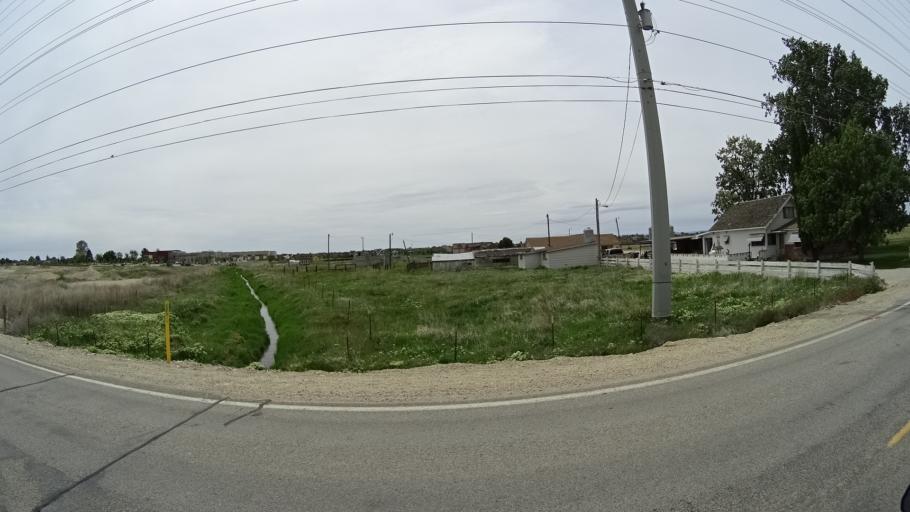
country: US
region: Idaho
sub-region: Ada County
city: Meridian
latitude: 43.5612
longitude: -116.3486
